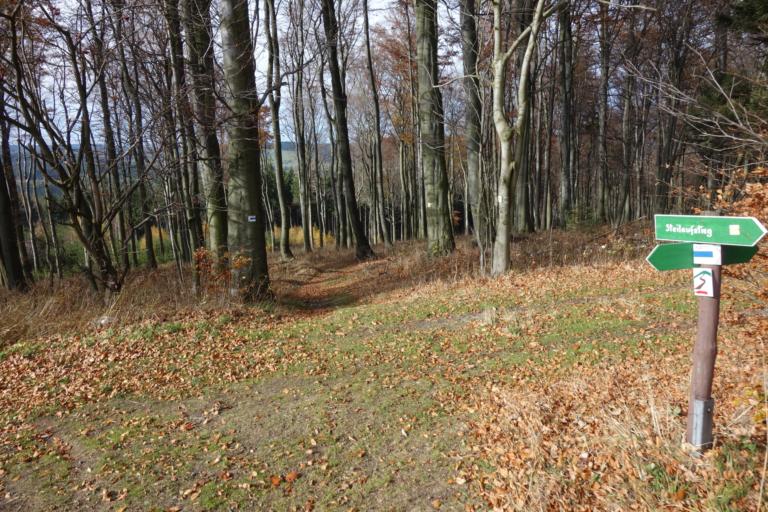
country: DE
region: Saxony
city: Barenstein
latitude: 50.5055
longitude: 13.0154
